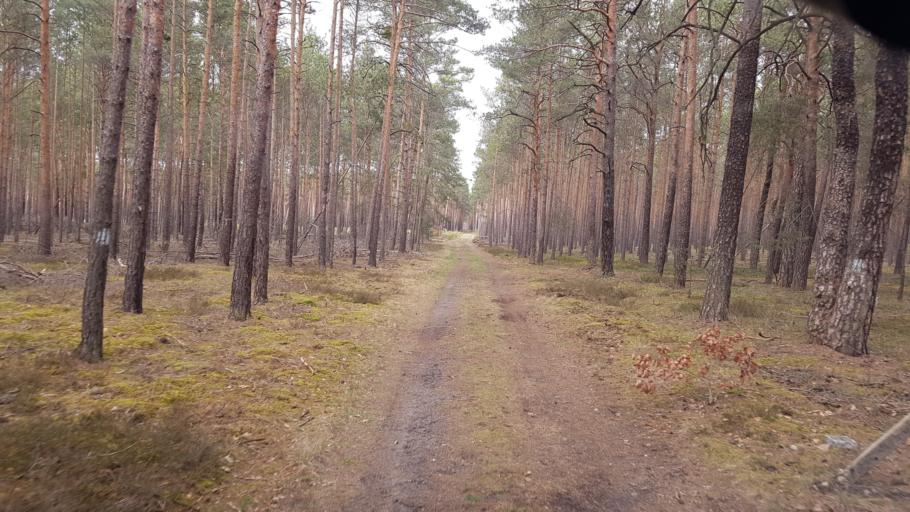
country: DE
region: Brandenburg
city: Finsterwalde
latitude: 51.5694
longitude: 13.6898
